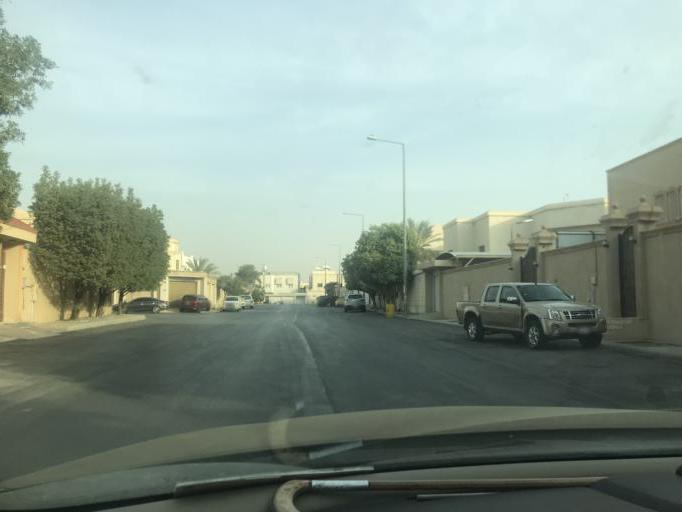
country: SA
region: Ar Riyad
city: Riyadh
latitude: 24.7433
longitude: 46.7520
